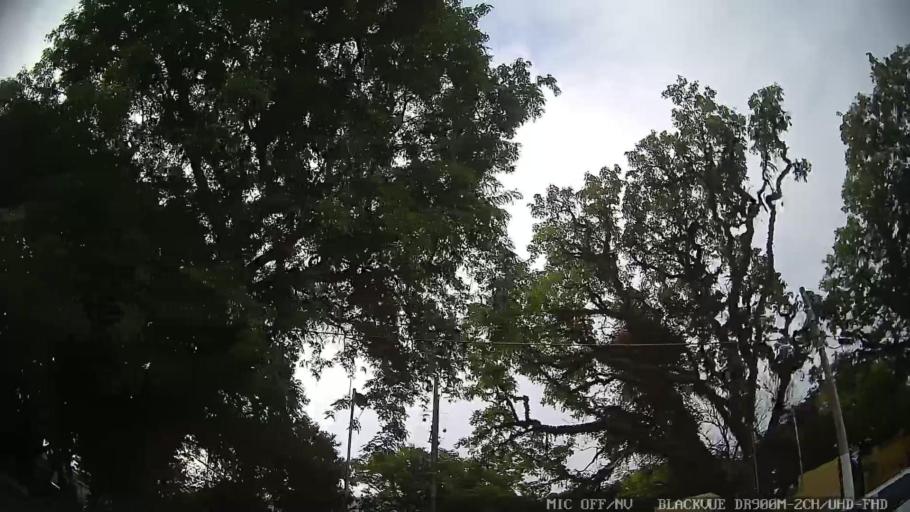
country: BR
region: Sao Paulo
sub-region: Braganca Paulista
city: Braganca Paulista
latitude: -22.9422
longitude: -46.5362
